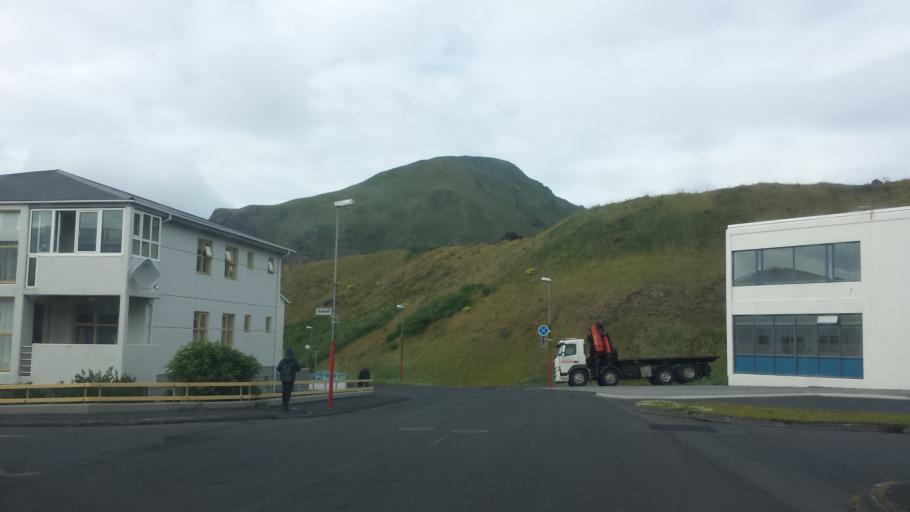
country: IS
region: South
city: Vestmannaeyjar
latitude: 63.4393
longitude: -20.2626
